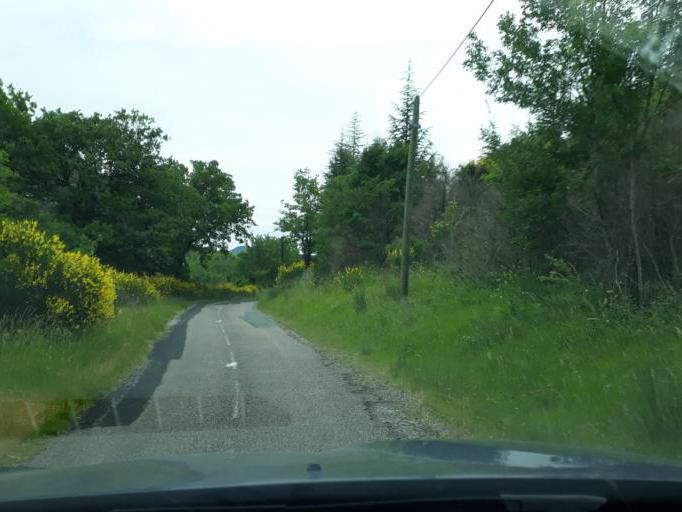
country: FR
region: Languedoc-Roussillon
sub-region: Departement de l'Herault
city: Lodeve
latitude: 43.7875
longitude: 3.2814
